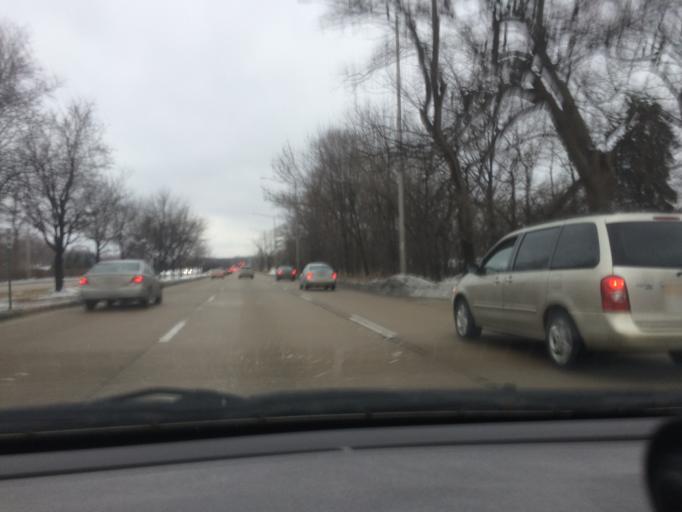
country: US
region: Illinois
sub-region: DuPage County
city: Bloomingdale
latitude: 41.9552
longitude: -88.0531
